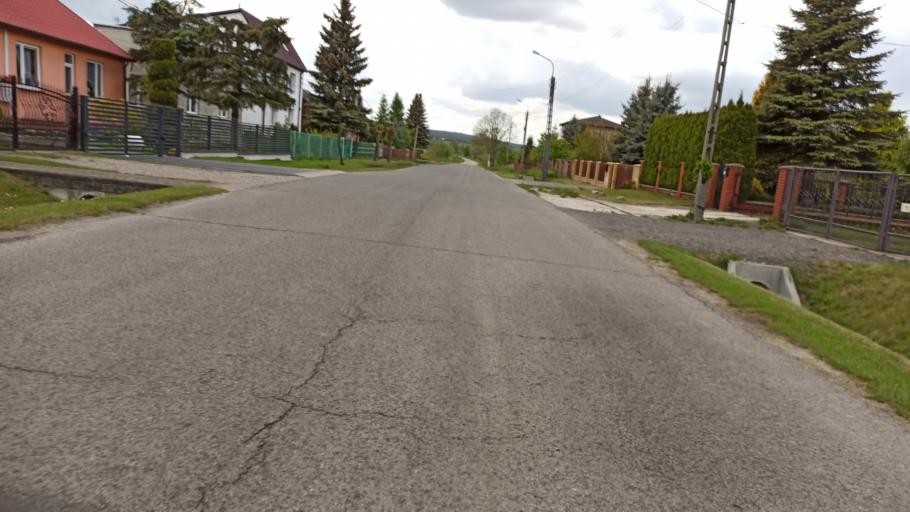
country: PL
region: Swietokrzyskie
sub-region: Powiat skarzyski
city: Skarzysko Koscielne
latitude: 51.1383
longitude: 20.9064
